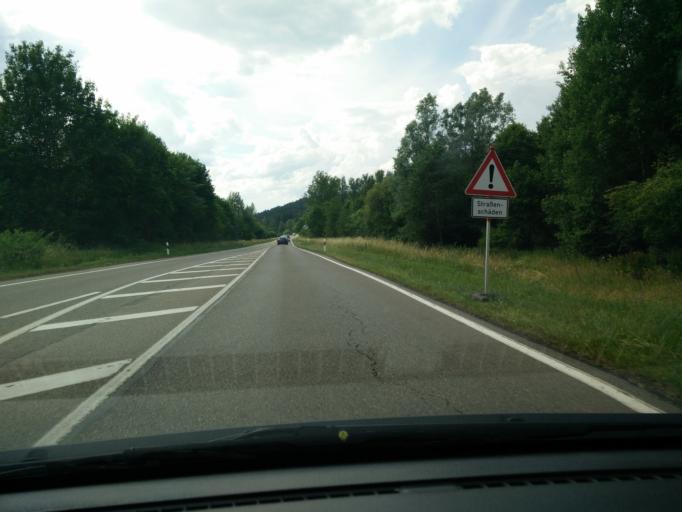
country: DE
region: Baden-Wuerttemberg
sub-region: Freiburg Region
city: Trossingen
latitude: 48.0789
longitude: 8.6178
